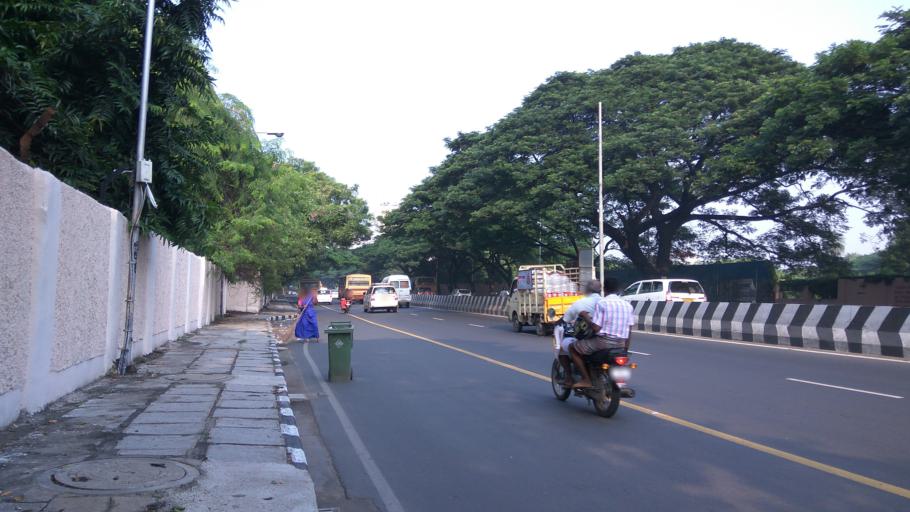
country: IN
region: Tamil Nadu
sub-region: Kancheepuram
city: Alandur
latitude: 13.0097
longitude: 80.2270
